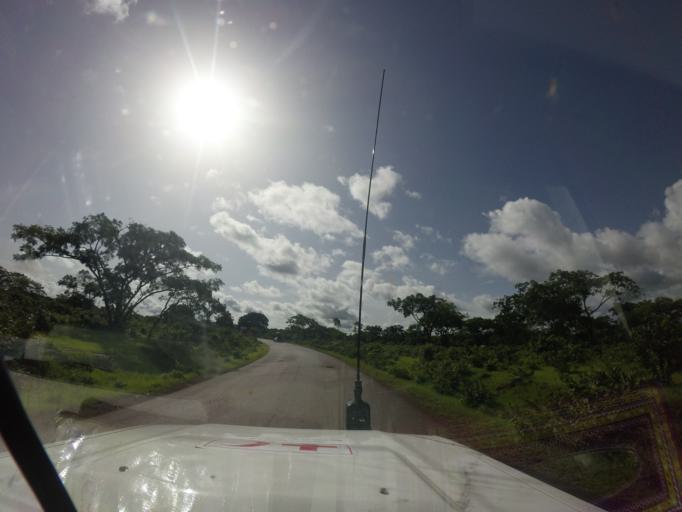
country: GN
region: Mamou
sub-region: Mamou Prefecture
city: Mamou
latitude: 10.2963
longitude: -12.3659
